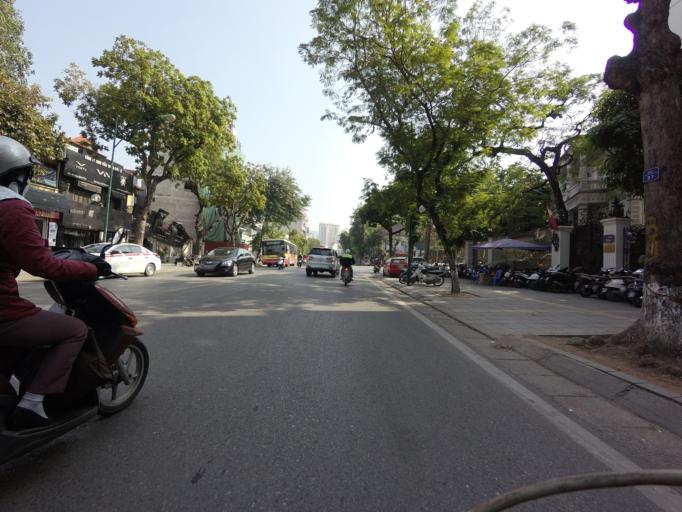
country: VN
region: Ha Noi
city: Hanoi
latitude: 21.0303
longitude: 105.8414
